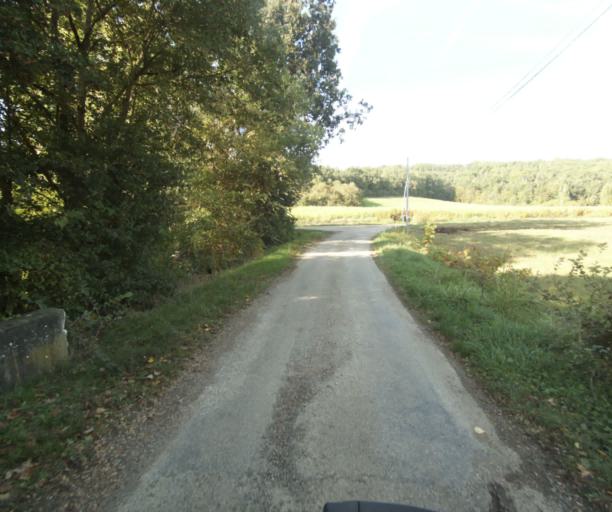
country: FR
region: Midi-Pyrenees
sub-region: Departement du Tarn-et-Garonne
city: Saint-Porquier
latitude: 43.9366
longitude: 1.1460
